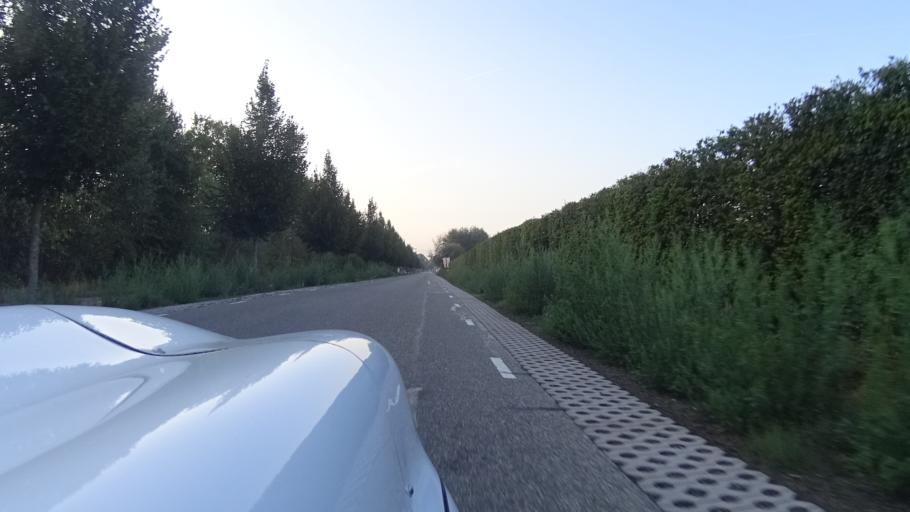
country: NL
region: North Brabant
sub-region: Gemeente Sint Anthonis
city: Sint Anthonis
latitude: 51.6096
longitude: 5.9090
